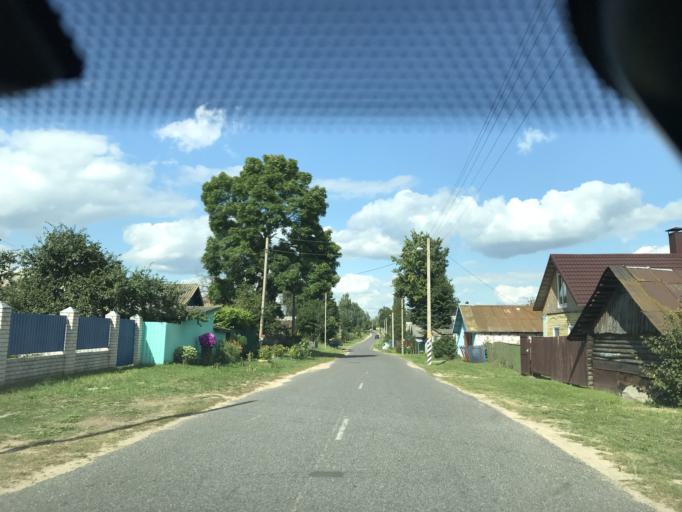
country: BY
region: Mogilev
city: Poselok Voskhod
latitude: 53.7872
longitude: 30.3557
